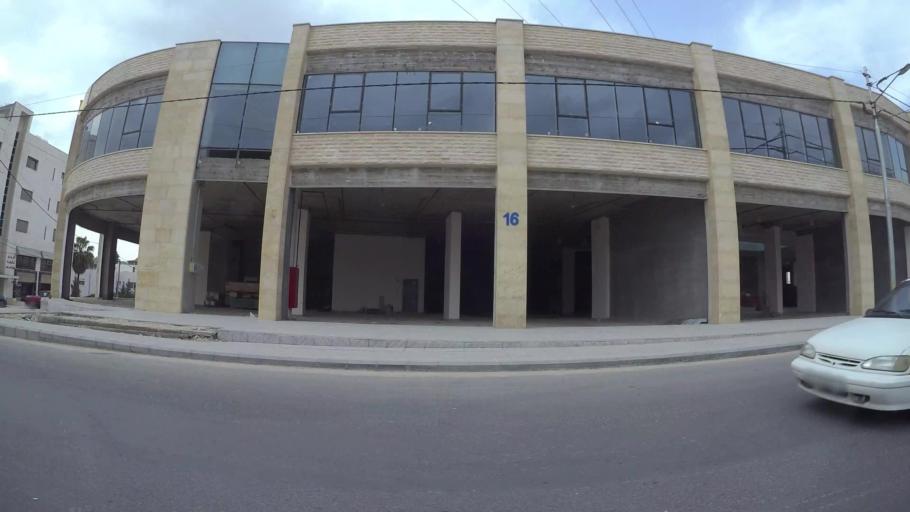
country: JO
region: Amman
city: Umm as Summaq
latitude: 31.8960
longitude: 35.8644
